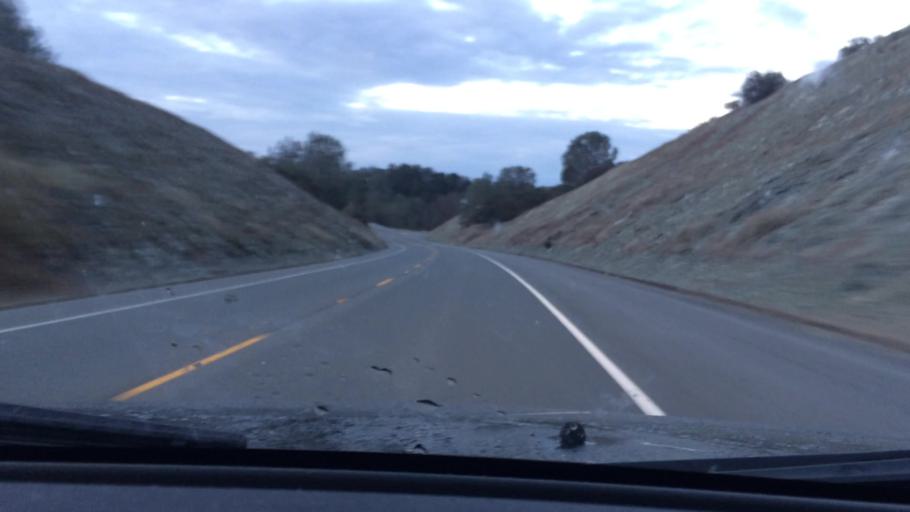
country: US
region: California
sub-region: Amador County
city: Ione
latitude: 38.4088
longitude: -120.8890
